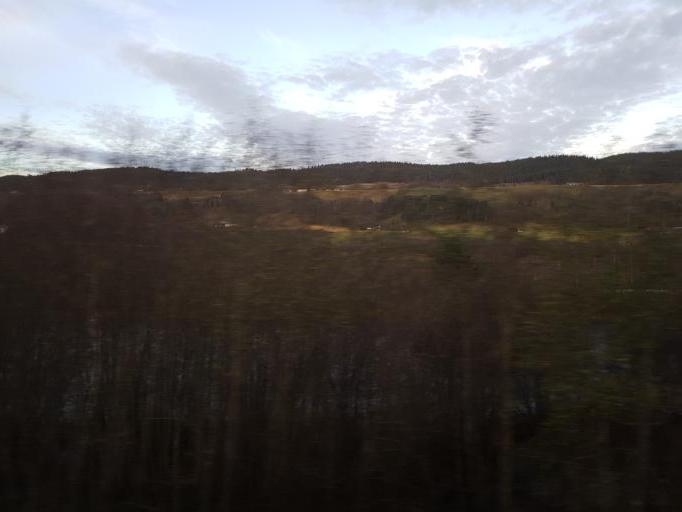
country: NO
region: Sor-Trondelag
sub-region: Melhus
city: Lundamo
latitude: 63.1186
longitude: 10.2420
